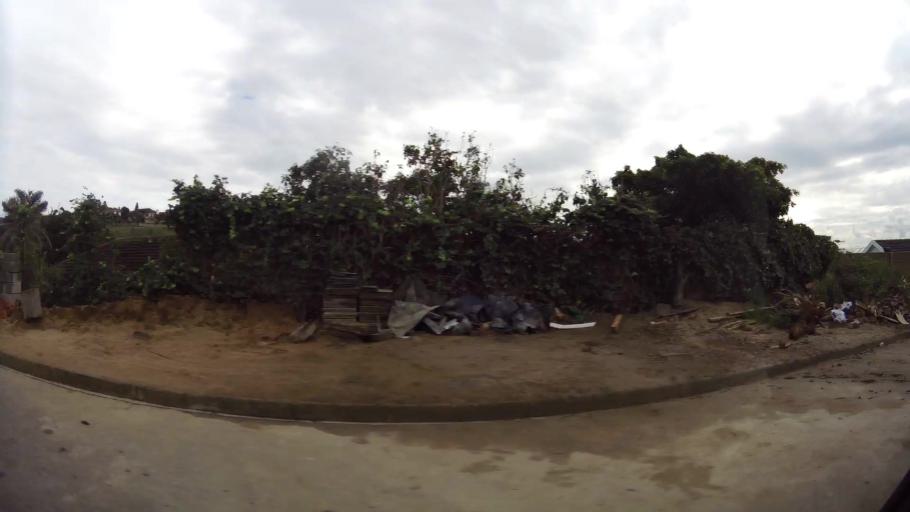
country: ZA
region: Eastern Cape
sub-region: Nelson Mandela Bay Metropolitan Municipality
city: Port Elizabeth
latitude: -33.9470
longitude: 25.5974
